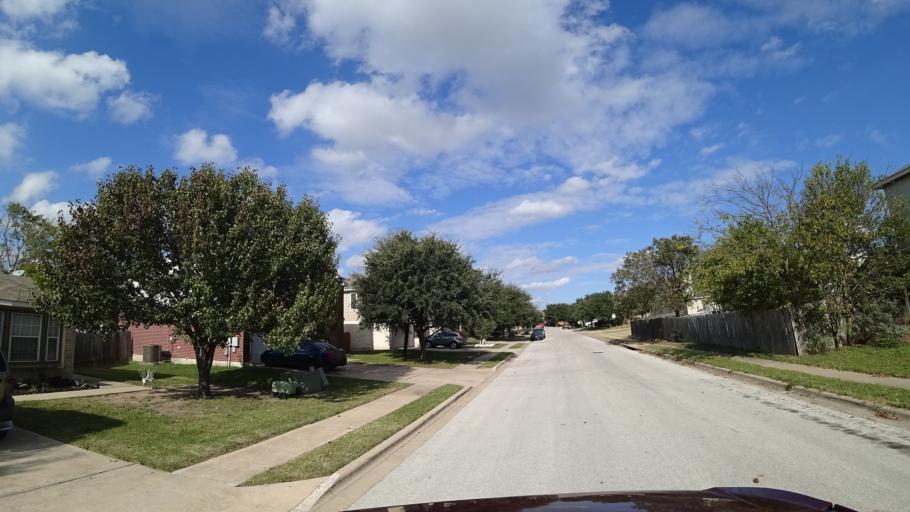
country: US
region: Texas
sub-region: Travis County
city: Pflugerville
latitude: 30.4311
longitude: -97.6399
